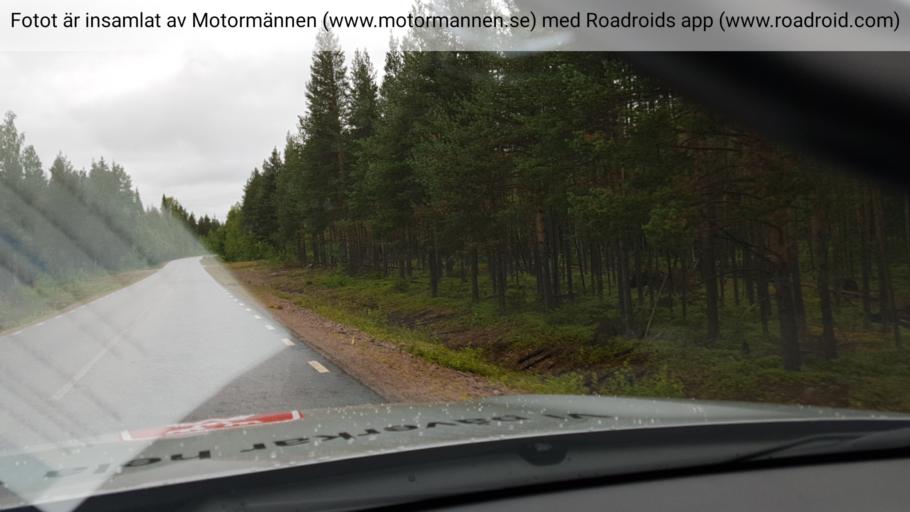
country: SE
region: Norrbotten
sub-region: Gallivare Kommun
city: Gaellivare
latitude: 66.6523
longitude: 20.3834
